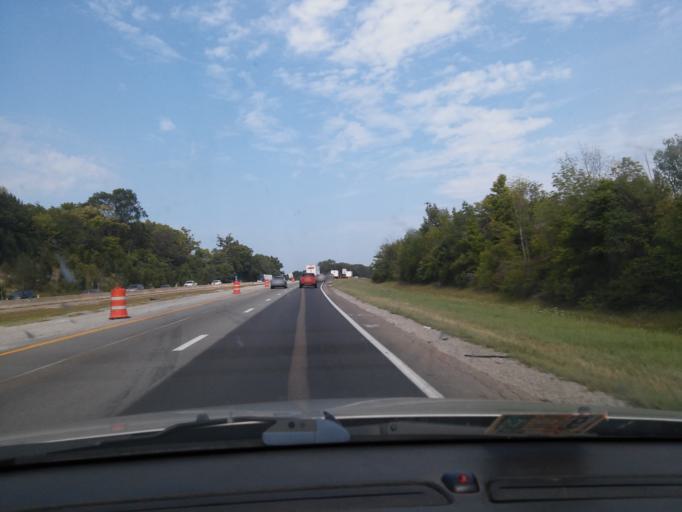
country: US
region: Ohio
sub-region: Montgomery County
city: Englewood
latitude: 39.8633
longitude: -84.2600
